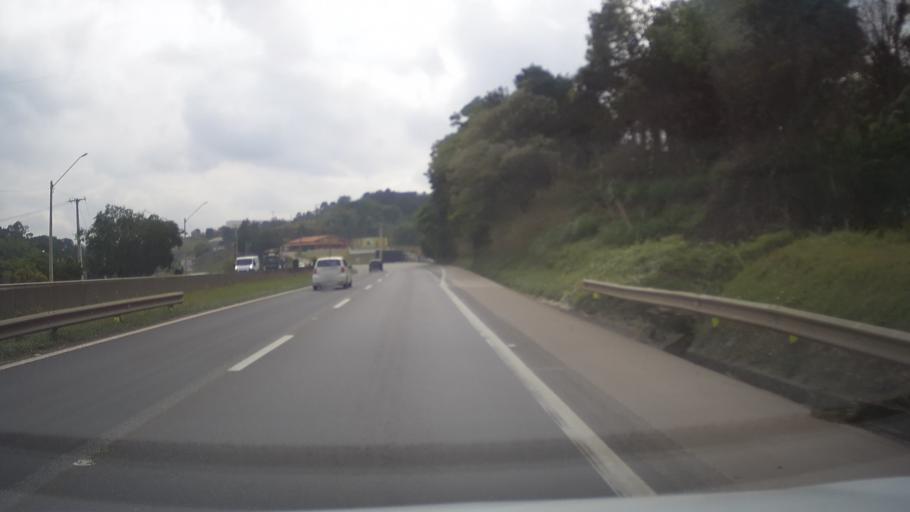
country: BR
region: Minas Gerais
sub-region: Extrema
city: Extrema
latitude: -22.8225
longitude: -46.3025
